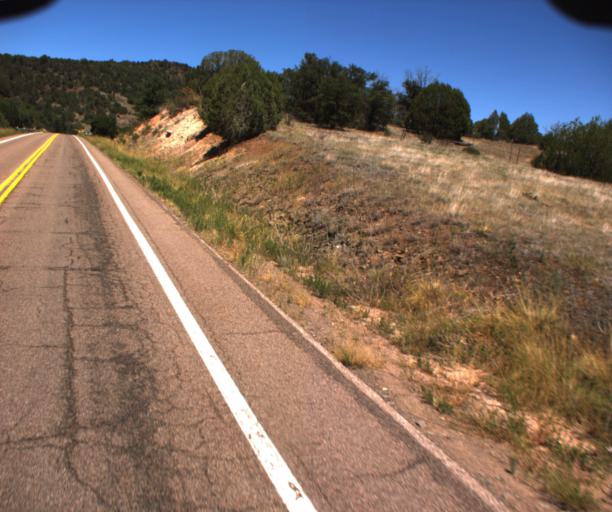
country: US
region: Arizona
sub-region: Navajo County
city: Cibecue
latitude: 33.9135
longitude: -110.3628
